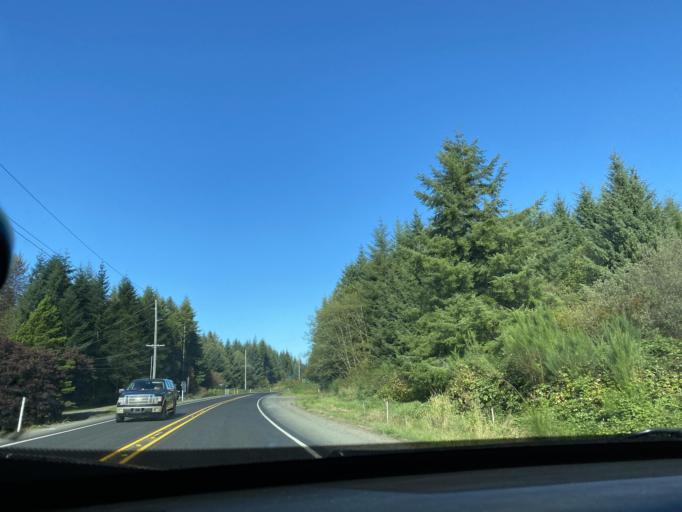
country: US
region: Washington
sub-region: Clallam County
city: Forks
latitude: 47.9634
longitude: -124.4000
